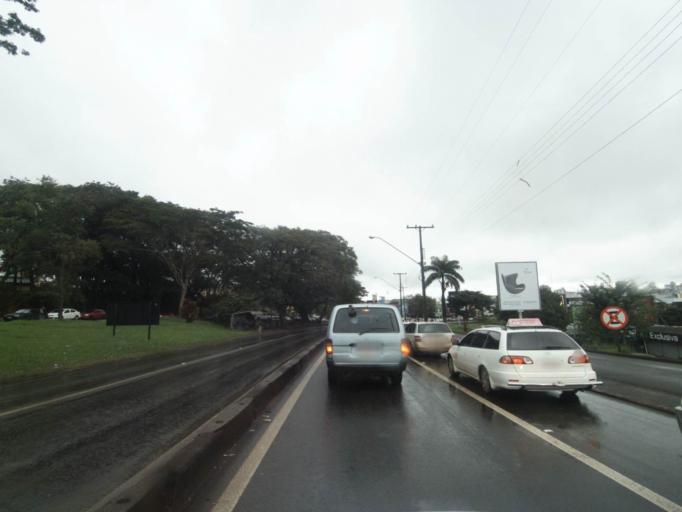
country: PY
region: Alto Parana
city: Ciudad del Este
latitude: -25.5083
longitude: -54.5924
